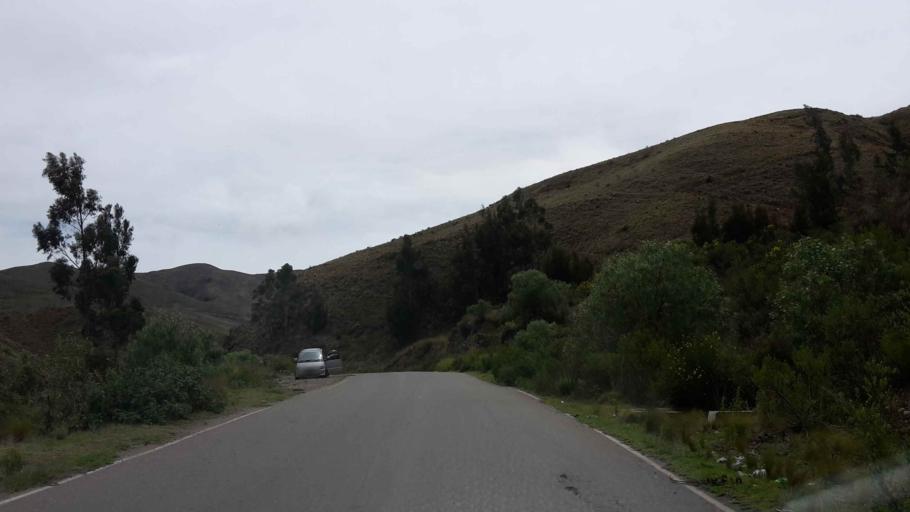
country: BO
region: Cochabamba
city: Colomi
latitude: -17.3992
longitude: -65.8043
